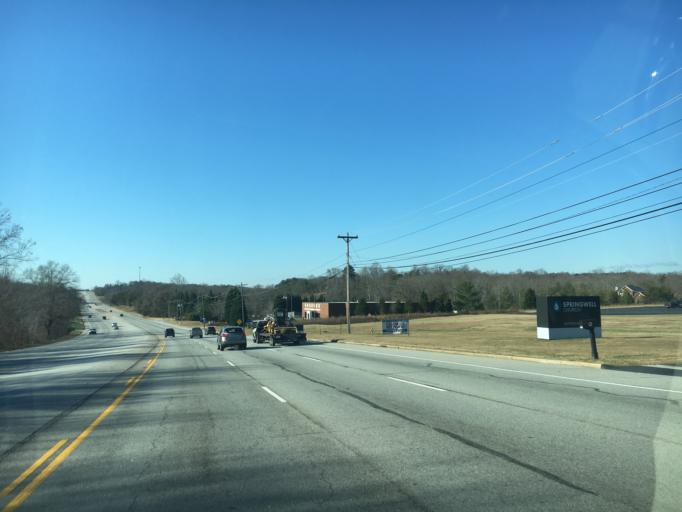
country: US
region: South Carolina
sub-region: Greenville County
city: Taylors
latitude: 34.9282
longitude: -82.2986
